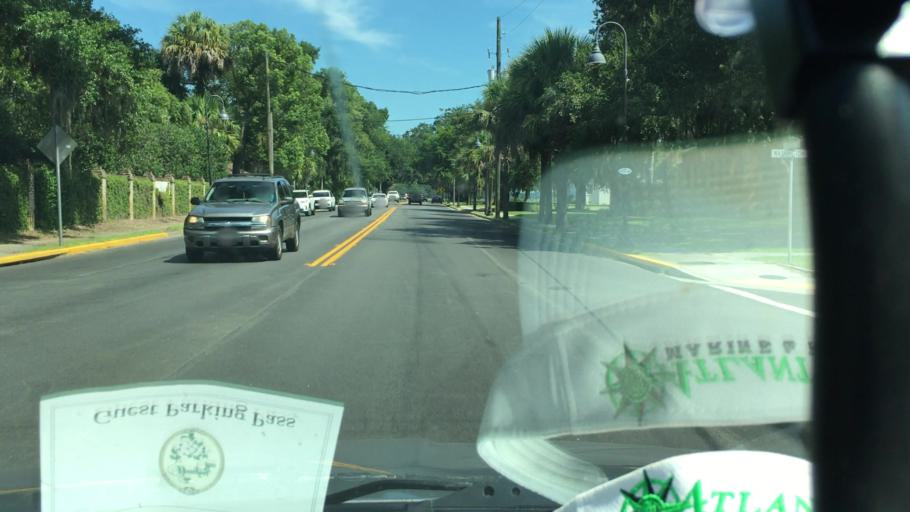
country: US
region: South Carolina
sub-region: Beaufort County
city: Beaufort
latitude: 32.4369
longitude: -80.6699
